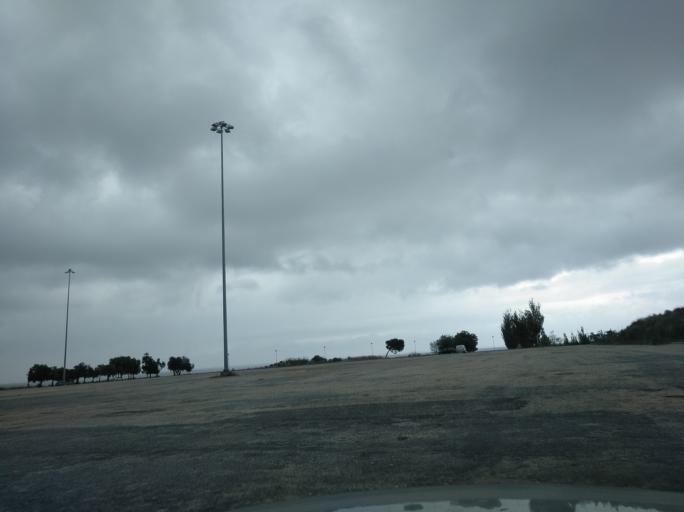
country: PT
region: Lisbon
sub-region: Loures
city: Bobadela
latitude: 38.7946
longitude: -9.0938
